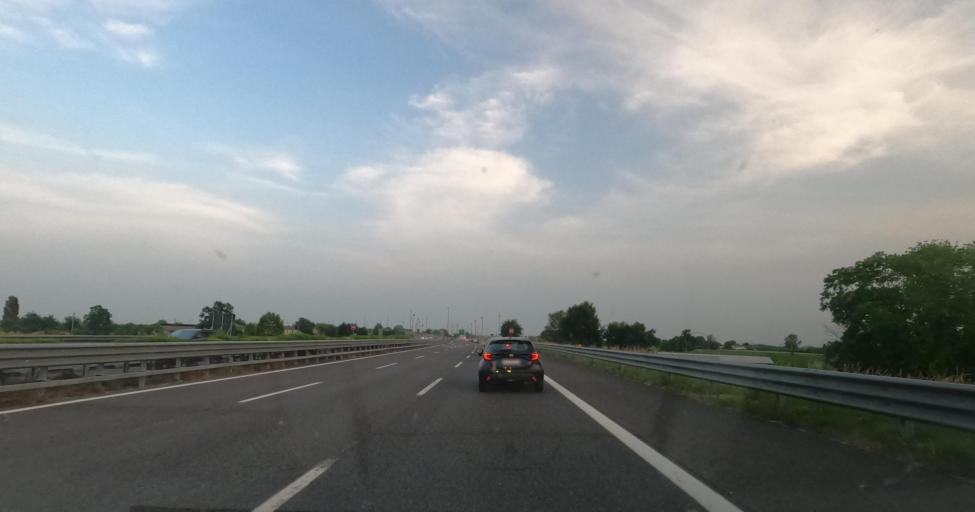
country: IT
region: Veneto
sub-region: Provincia di Treviso
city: Mogliano Veneto
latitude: 45.5433
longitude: 12.2729
